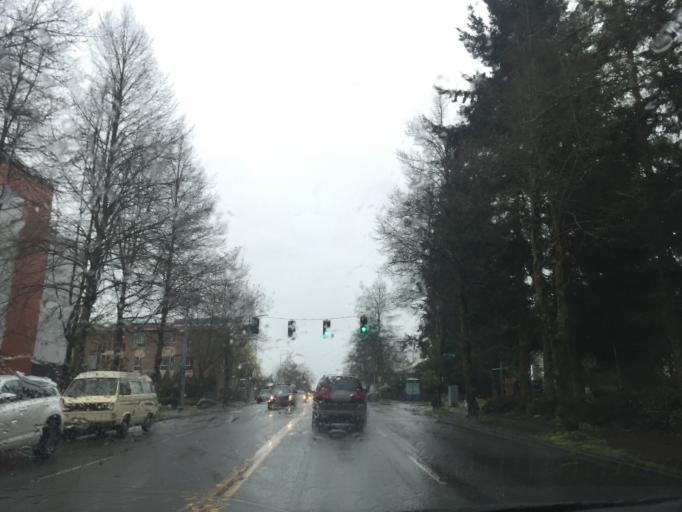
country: US
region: Washington
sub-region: King County
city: Shoreline
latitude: 47.7218
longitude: -122.3127
